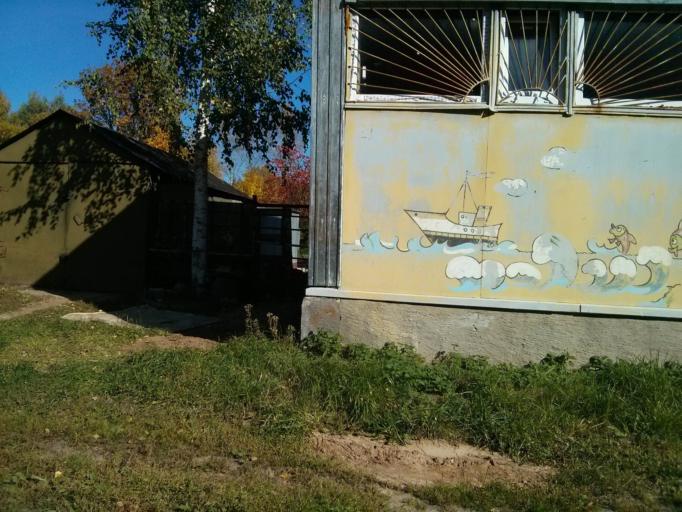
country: RU
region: Vladimir
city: Murom
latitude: 55.5483
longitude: 42.0598
